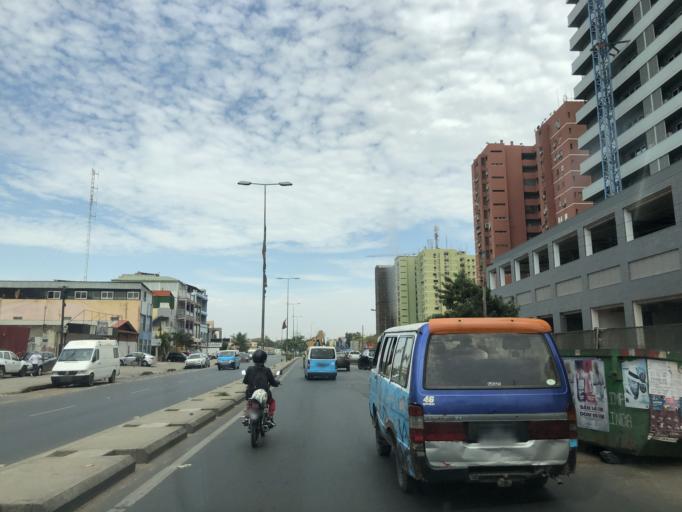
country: AO
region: Luanda
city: Luanda
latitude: -8.8244
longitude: 13.2546
